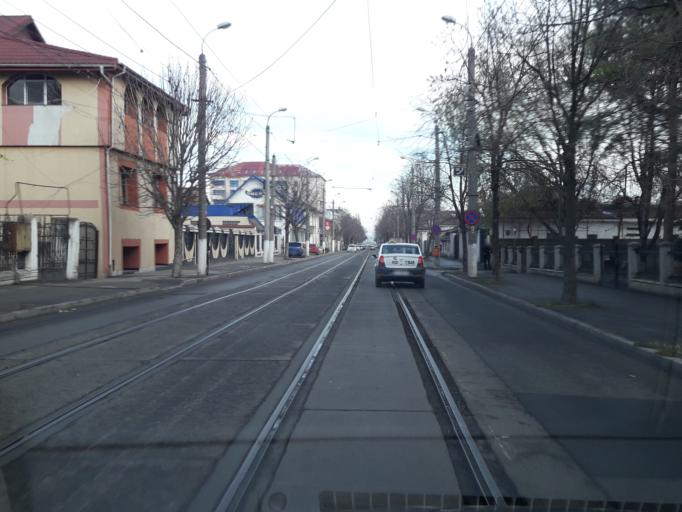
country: RO
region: Galati
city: Galati
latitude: 45.4444
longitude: 28.0488
